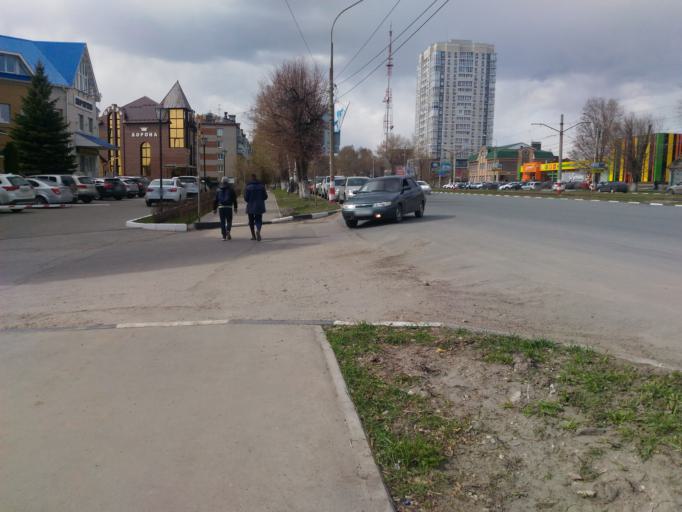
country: RU
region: Ulyanovsk
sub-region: Ulyanovskiy Rayon
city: Ulyanovsk
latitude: 54.3339
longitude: 48.3843
